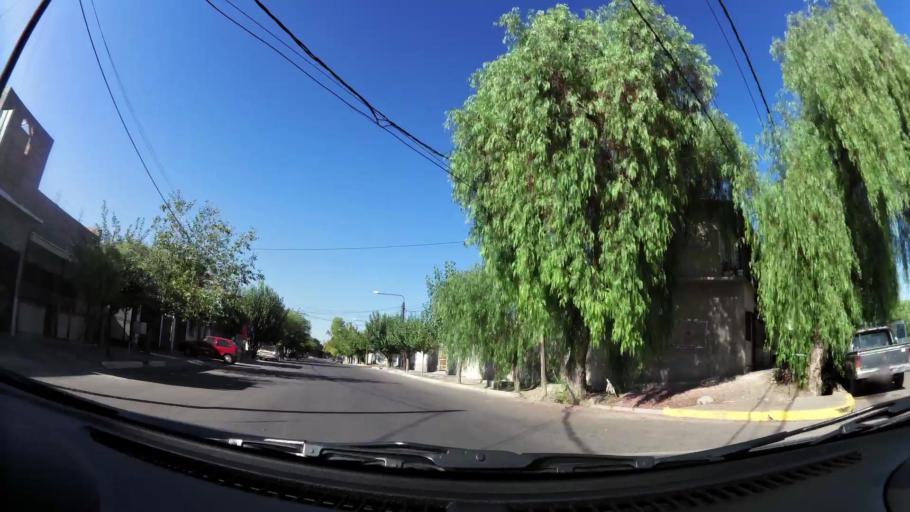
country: AR
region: Mendoza
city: Las Heras
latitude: -32.8730
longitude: -68.8692
